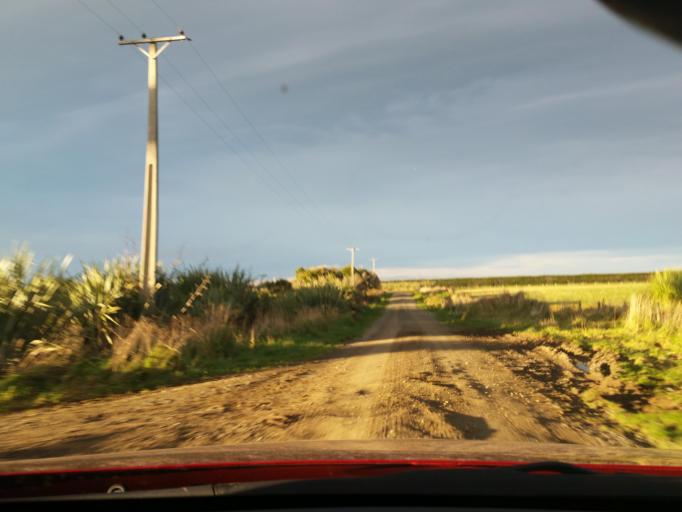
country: NZ
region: Southland
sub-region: Southland District
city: Riverton
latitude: -46.3199
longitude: 168.0950
